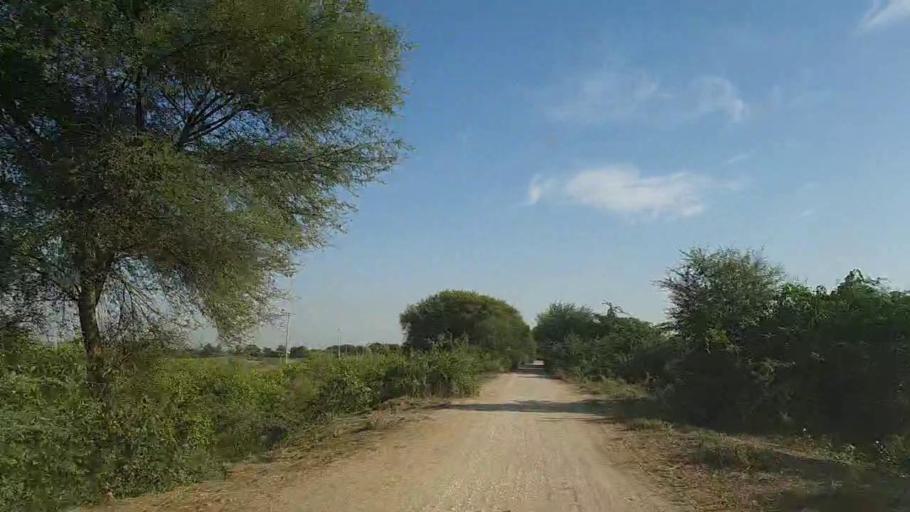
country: PK
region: Sindh
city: Bulri
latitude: 24.7798
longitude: 68.3547
